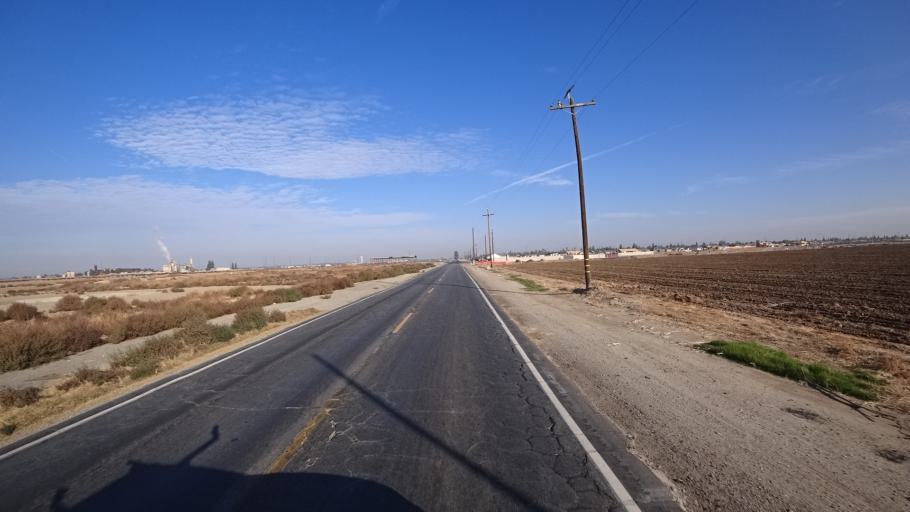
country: US
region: California
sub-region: Kern County
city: Greenfield
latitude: 35.2902
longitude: -119.0921
